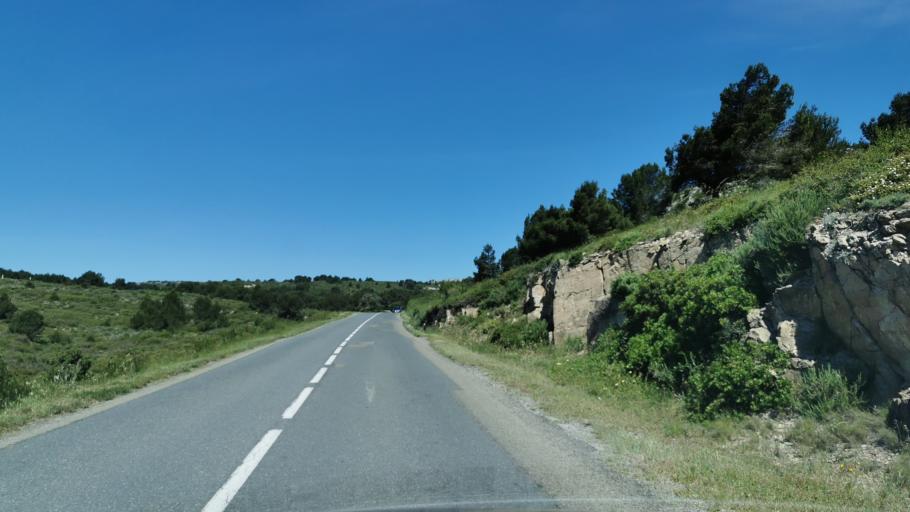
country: FR
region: Languedoc-Roussillon
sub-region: Departement de l'Aude
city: Armissan
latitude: 43.1607
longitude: 3.1466
